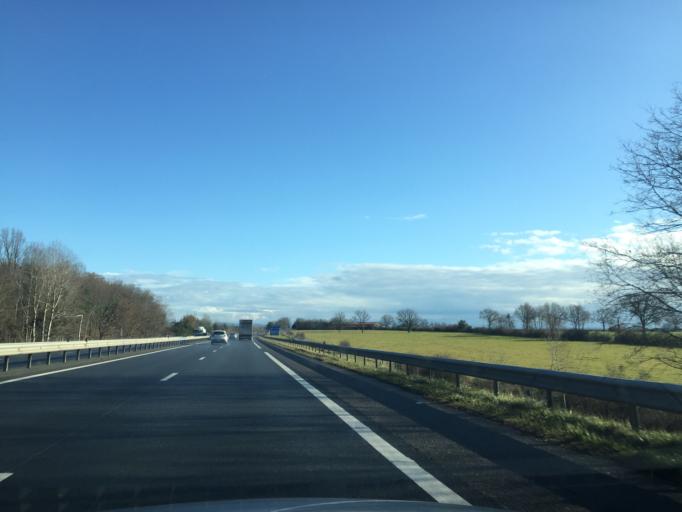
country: FR
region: Rhone-Alpes
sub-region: Departement de la Loire
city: Saint-Germain-Laval
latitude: 45.8525
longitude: 4.0653
